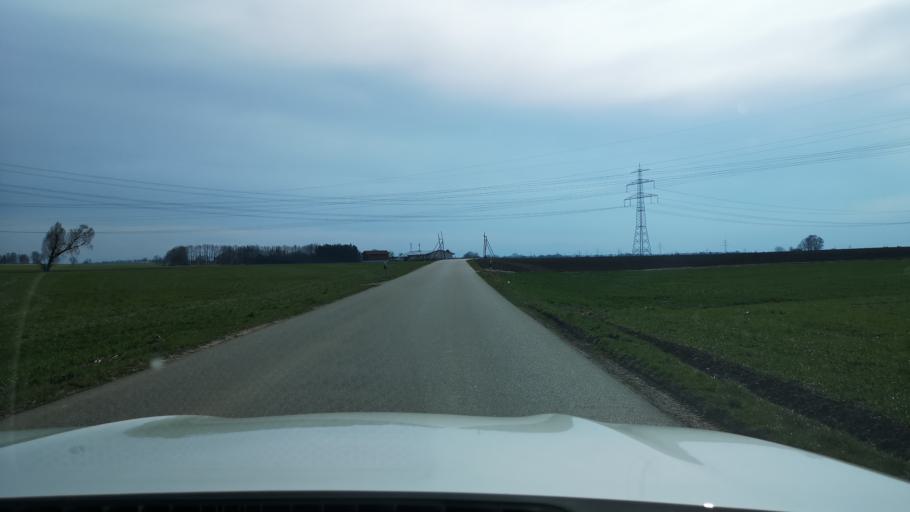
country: DE
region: Bavaria
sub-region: Upper Bavaria
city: Finsing
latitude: 48.2108
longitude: 11.8193
